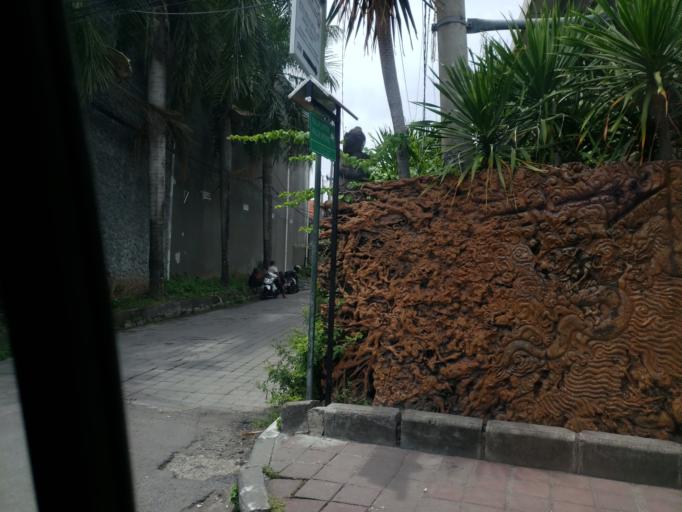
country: ID
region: Bali
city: Kuta
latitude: -8.6772
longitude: 115.1540
